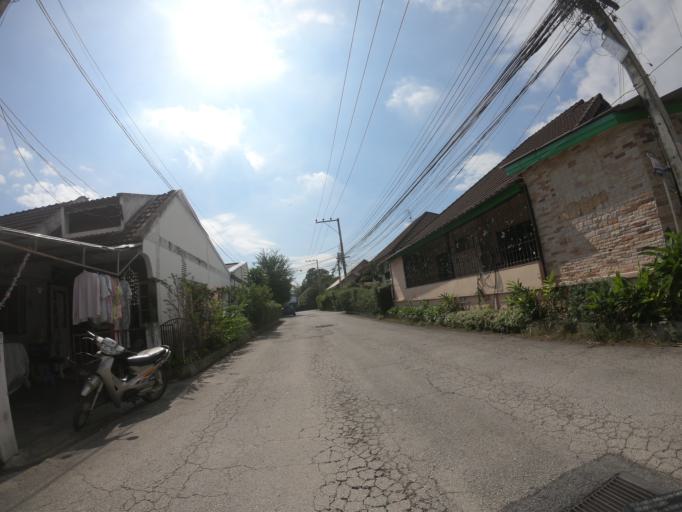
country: TH
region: Chiang Mai
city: Chiang Mai
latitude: 18.7361
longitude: 98.9611
